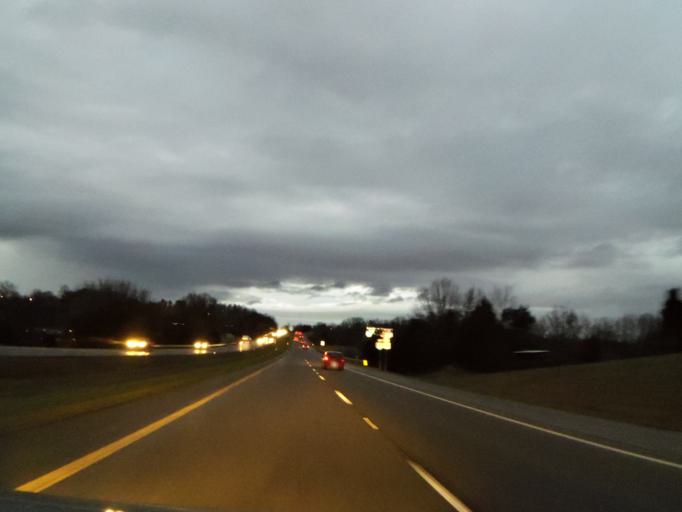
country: US
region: Tennessee
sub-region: Washington County
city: Gray
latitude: 36.4121
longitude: -82.4852
